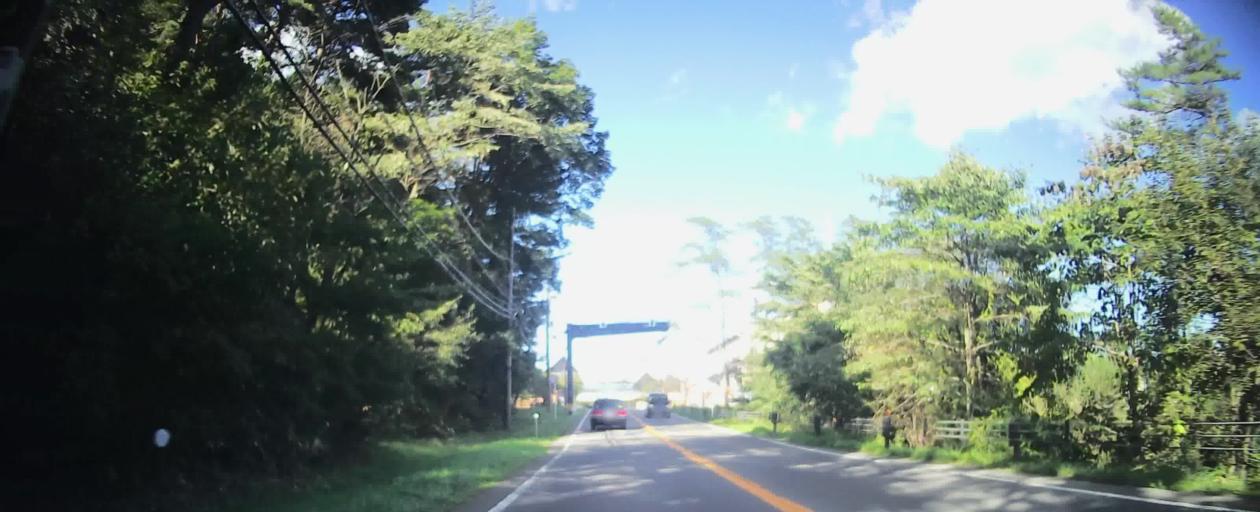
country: JP
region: Gunma
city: Nakanojomachi
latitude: 36.6133
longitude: 138.5894
